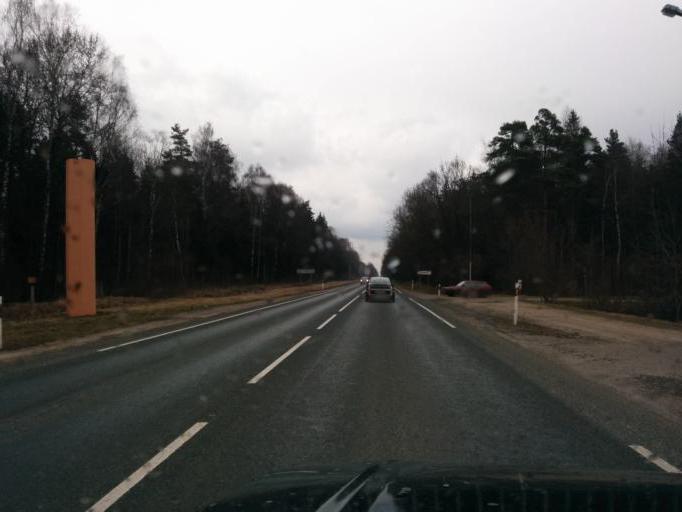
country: LV
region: Ozolnieku
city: Ozolnieki
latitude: 56.6956
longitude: 23.8036
